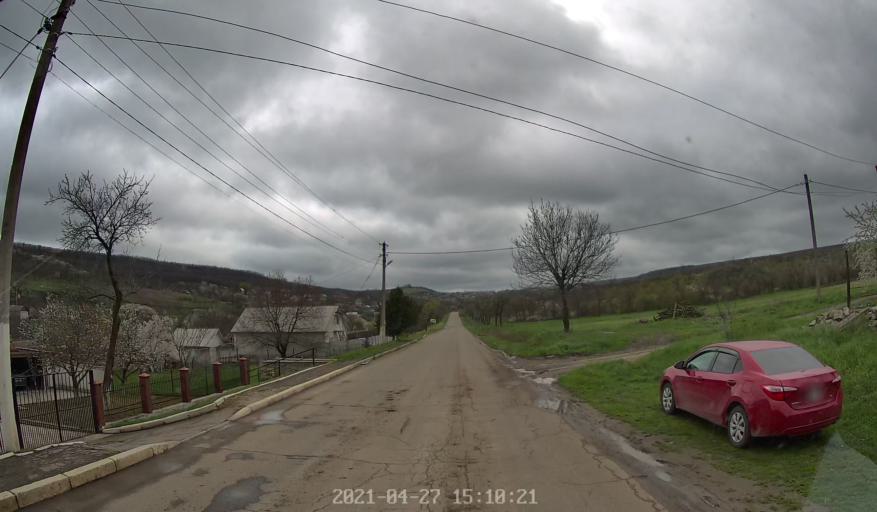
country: MD
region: Chisinau
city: Vadul lui Voda
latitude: 47.0414
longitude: 29.0329
